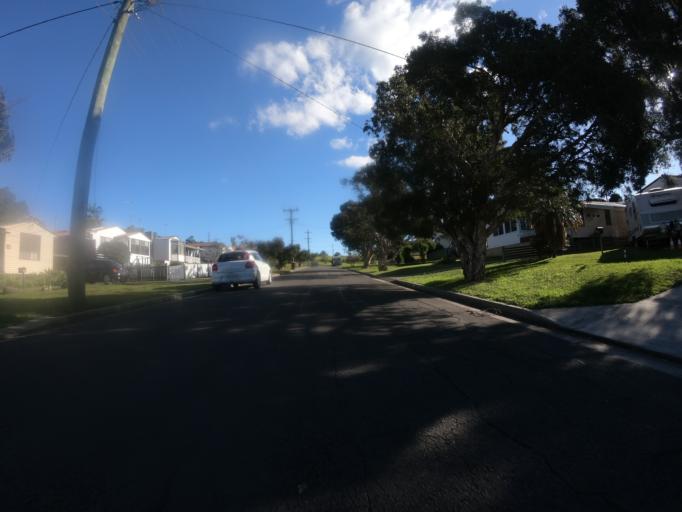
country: AU
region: New South Wales
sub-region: Wollongong
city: Cordeaux Heights
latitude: -34.4633
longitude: 150.8333
